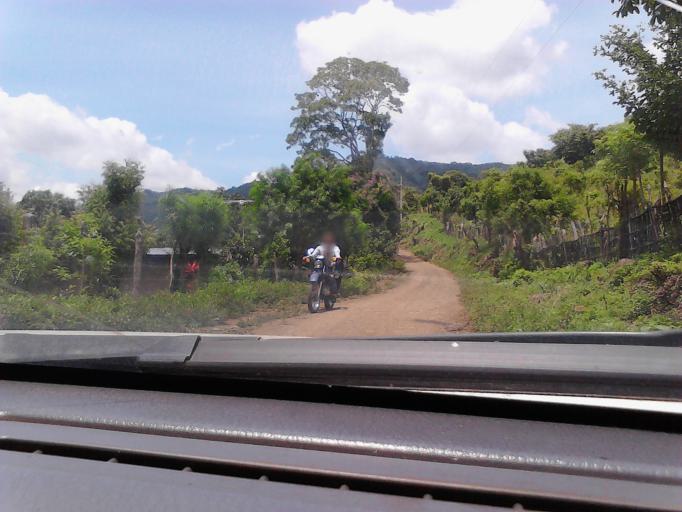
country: NI
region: Matagalpa
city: Terrabona
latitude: 12.7098
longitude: -85.9441
